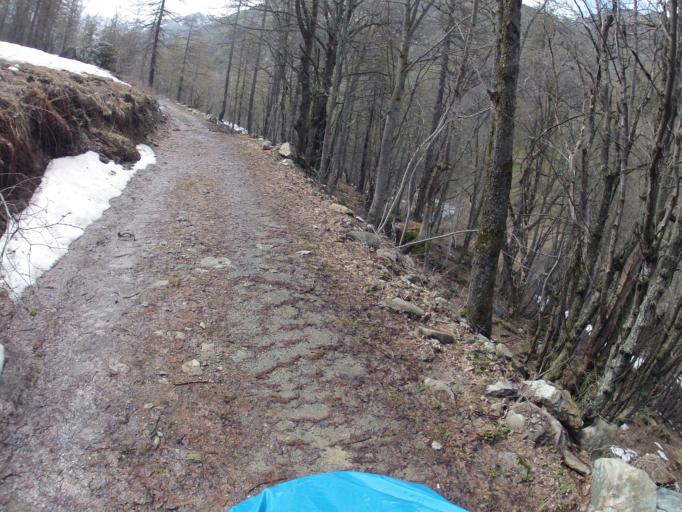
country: IT
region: Piedmont
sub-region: Provincia di Cuneo
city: Crissolo
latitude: 44.7012
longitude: 7.1413
